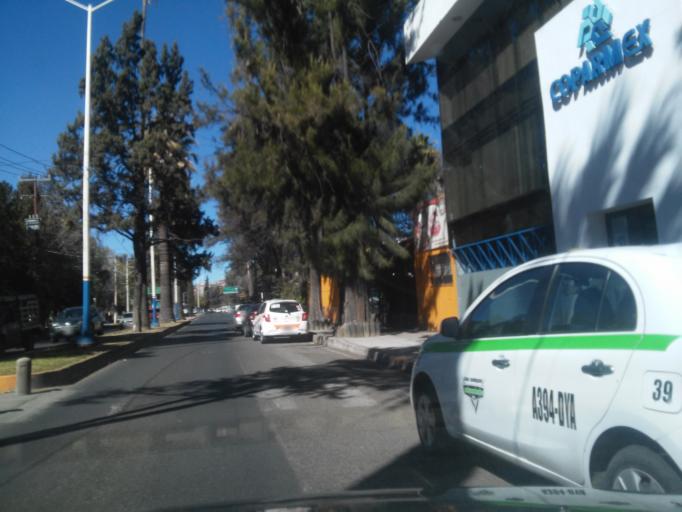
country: MX
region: Durango
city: Victoria de Durango
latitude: 24.0253
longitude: -104.6811
